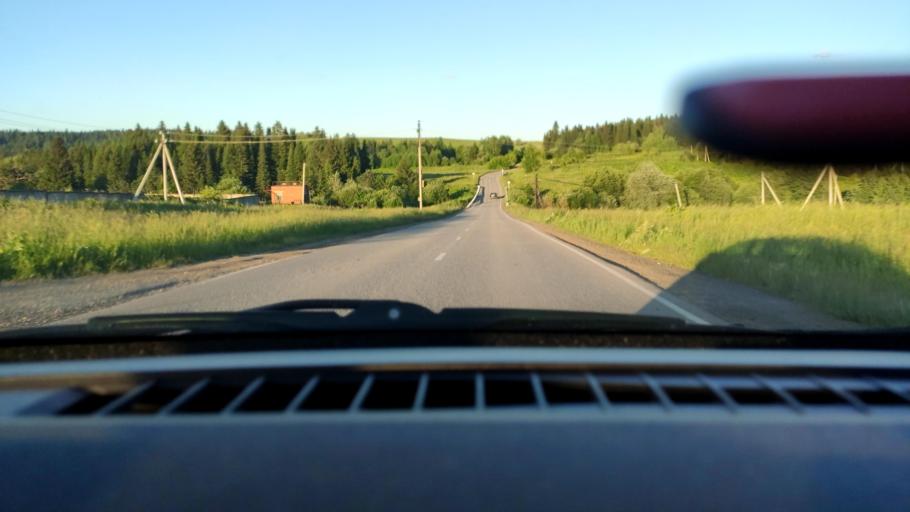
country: RU
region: Perm
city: Kultayevo
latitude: 57.9225
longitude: 55.9194
